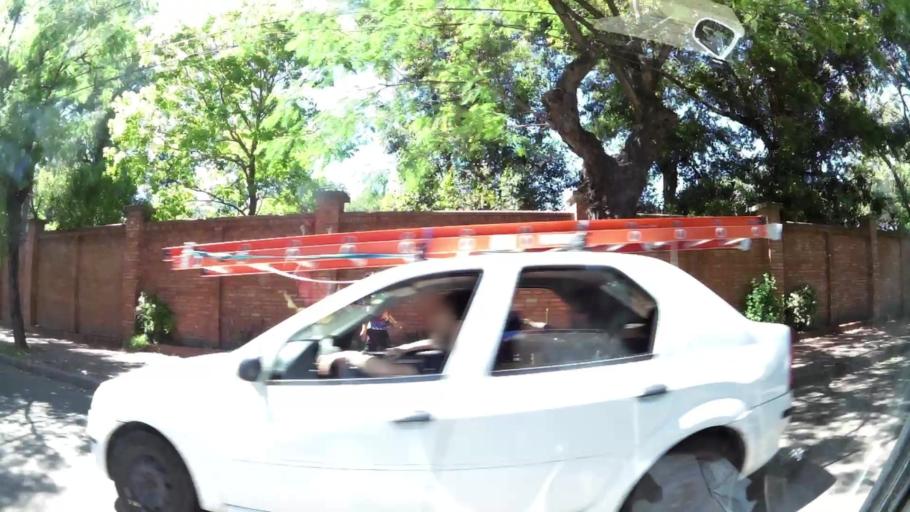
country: AR
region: Buenos Aires
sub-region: Partido de Vicente Lopez
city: Olivos
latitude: -34.5140
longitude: -58.4842
